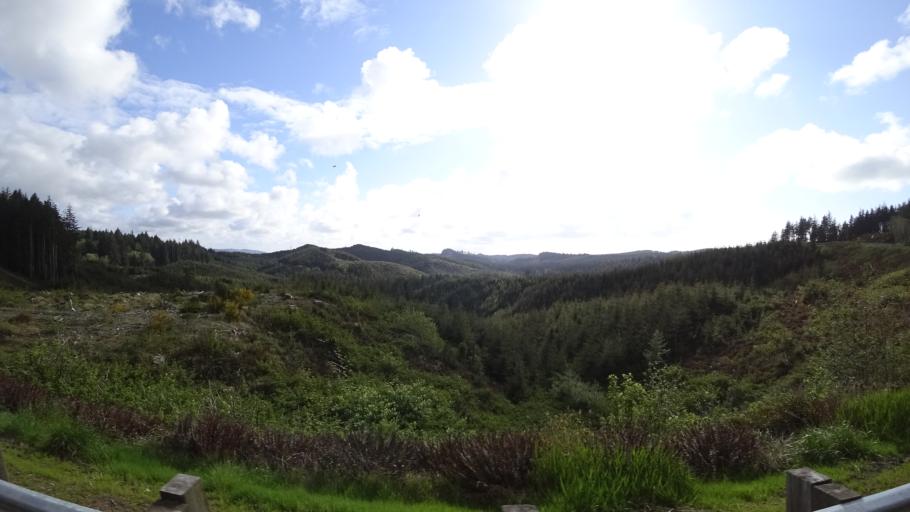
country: US
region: Oregon
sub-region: Douglas County
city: Reedsport
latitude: 43.7614
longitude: -124.1234
